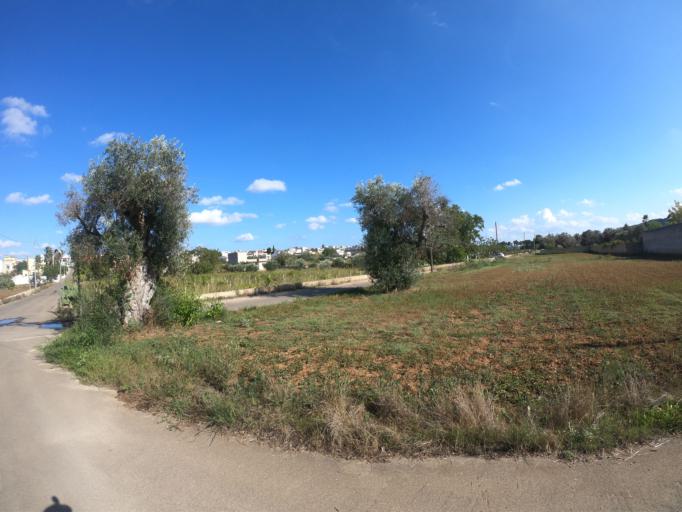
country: IT
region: Apulia
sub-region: Provincia di Lecce
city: Supersano
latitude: 40.0135
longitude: 18.2376
